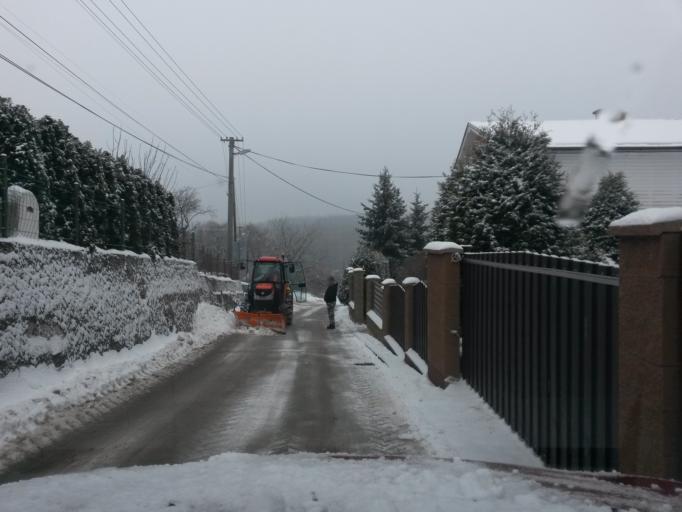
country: SK
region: Kosicky
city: Kosice
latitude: 48.7260
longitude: 21.3027
